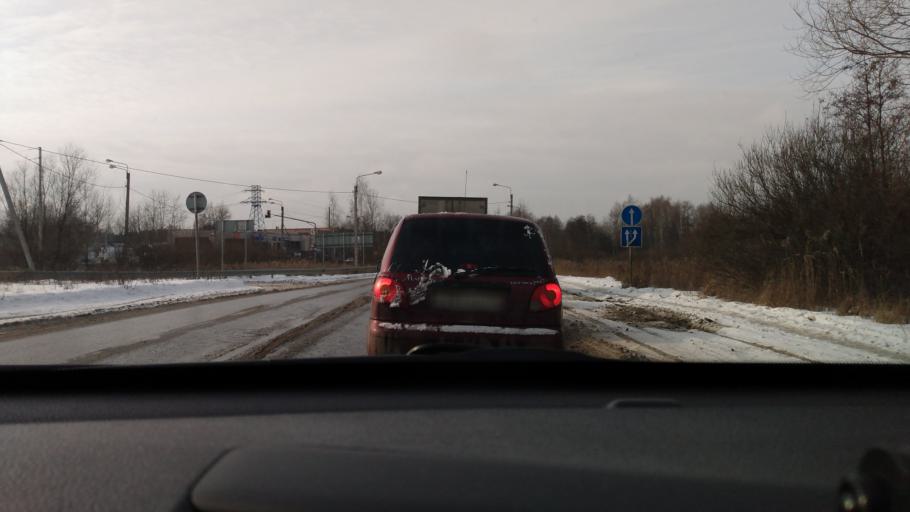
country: RU
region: Moskovskaya
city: Chornaya
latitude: 55.7514
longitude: 38.0584
